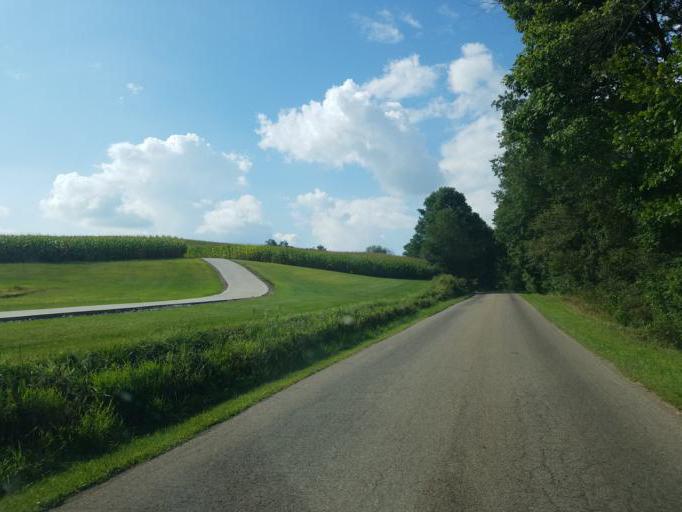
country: US
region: Ohio
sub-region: Knox County
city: Danville
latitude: 40.4707
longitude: -82.2985
